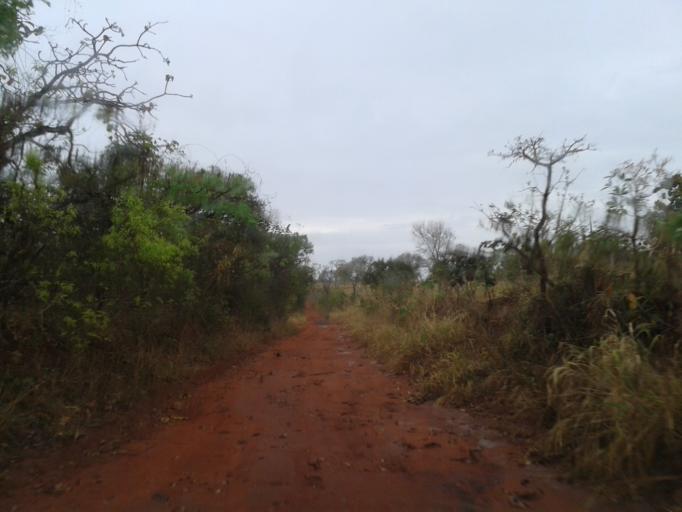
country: BR
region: Minas Gerais
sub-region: Campina Verde
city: Campina Verde
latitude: -19.3370
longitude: -49.5207
